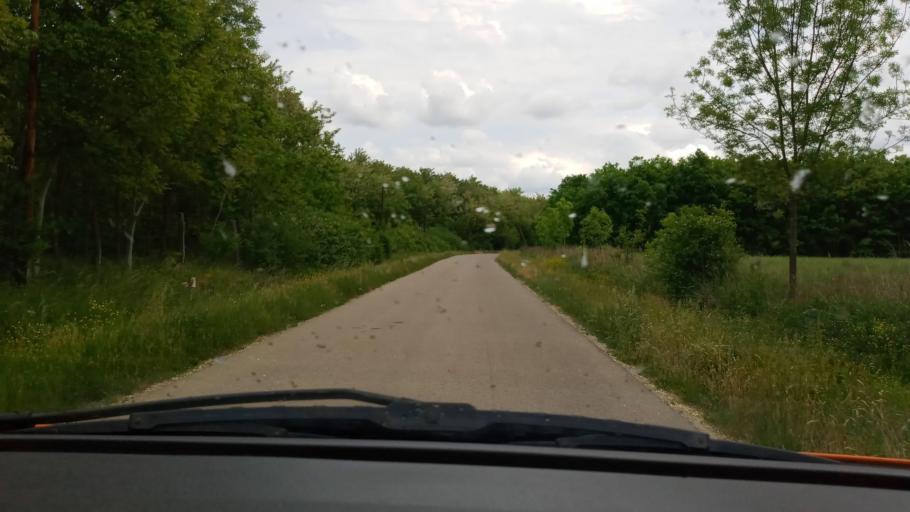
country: HU
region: Baranya
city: Vajszlo
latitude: 45.8288
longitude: 17.9775
